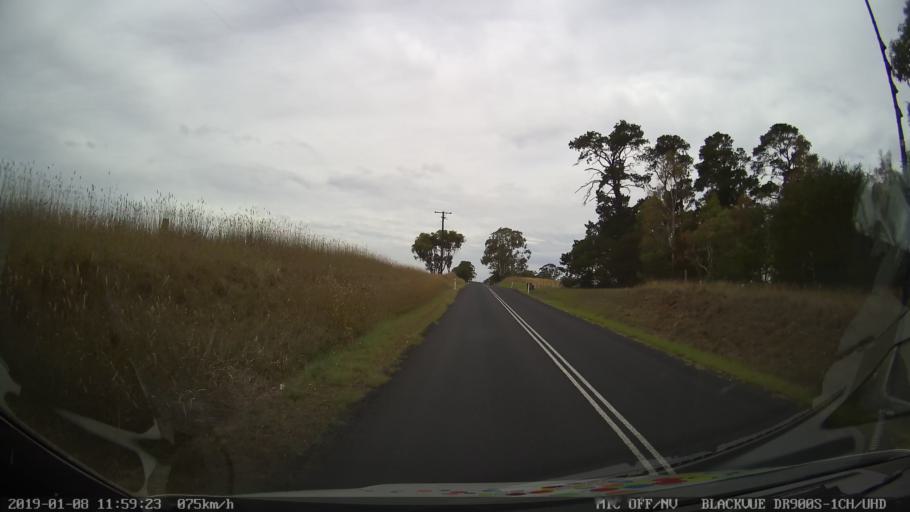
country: AU
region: New South Wales
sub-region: Armidale Dumaresq
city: Armidale
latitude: -30.4584
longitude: 151.5867
